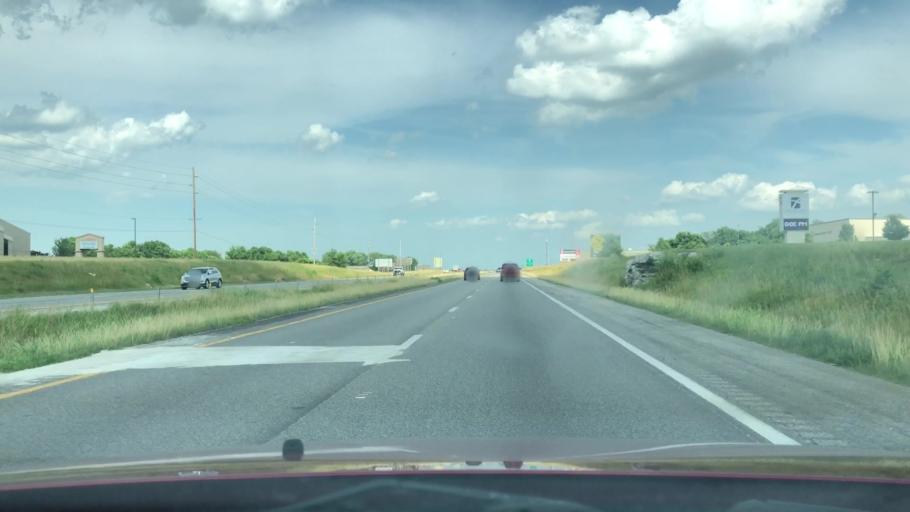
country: US
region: Missouri
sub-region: Greene County
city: Springfield
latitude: 37.2502
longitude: -93.2513
